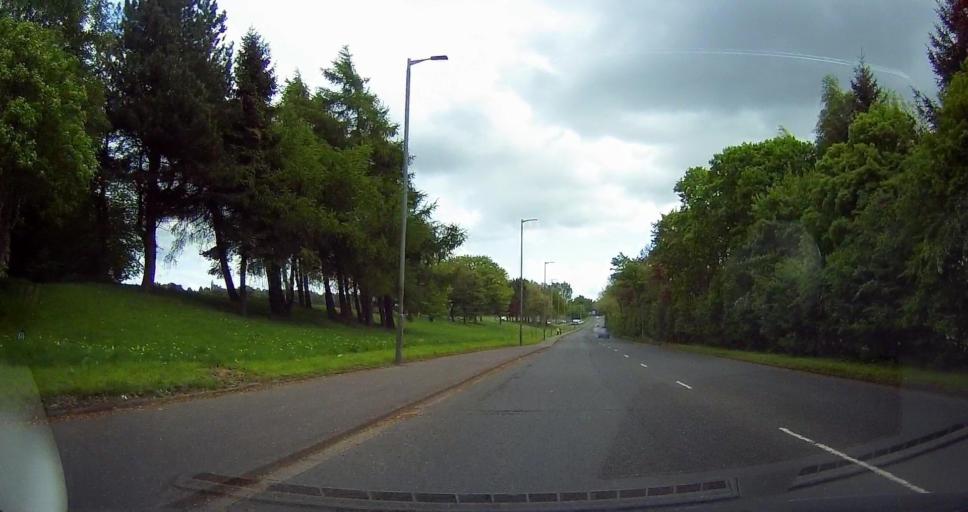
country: GB
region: Scotland
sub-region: Falkirk
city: Larbert
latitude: 56.0109
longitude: -3.8206
